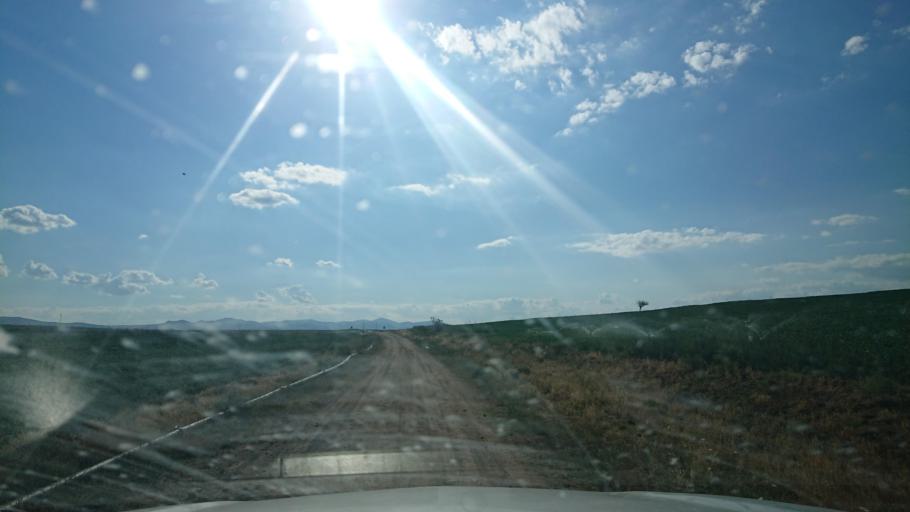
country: TR
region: Aksaray
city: Sariyahsi
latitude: 39.0196
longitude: 33.8903
